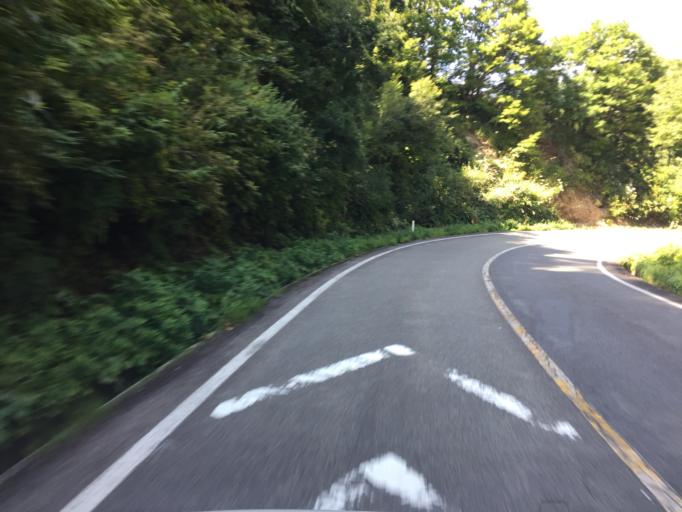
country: JP
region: Fukushima
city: Inawashiro
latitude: 37.6740
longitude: 140.1461
